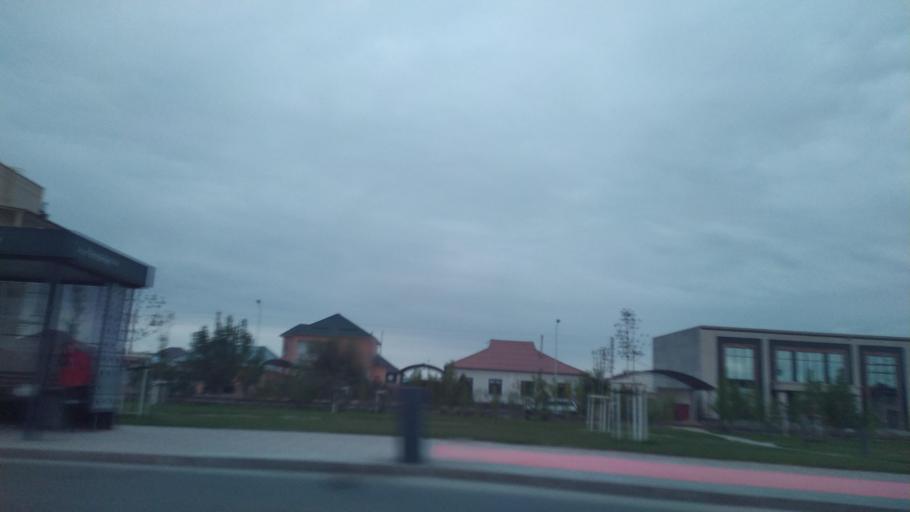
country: KZ
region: Ongtustik Qazaqstan
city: Turkestan
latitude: 43.2821
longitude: 68.3163
